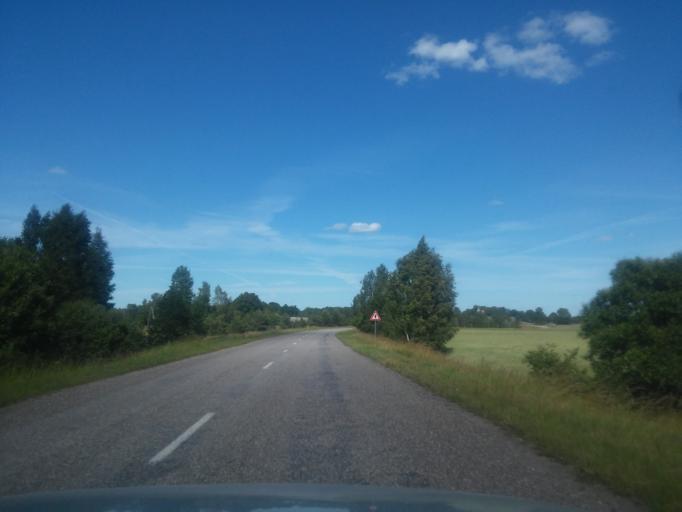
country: LV
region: Skrunda
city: Skrunda
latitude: 56.6225
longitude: 21.9691
